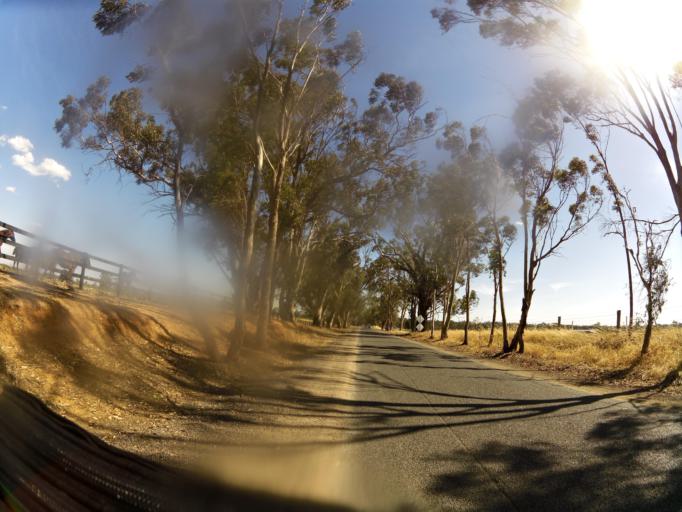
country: AU
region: Victoria
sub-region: Campaspe
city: Kyabram
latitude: -36.8611
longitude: 145.0882
